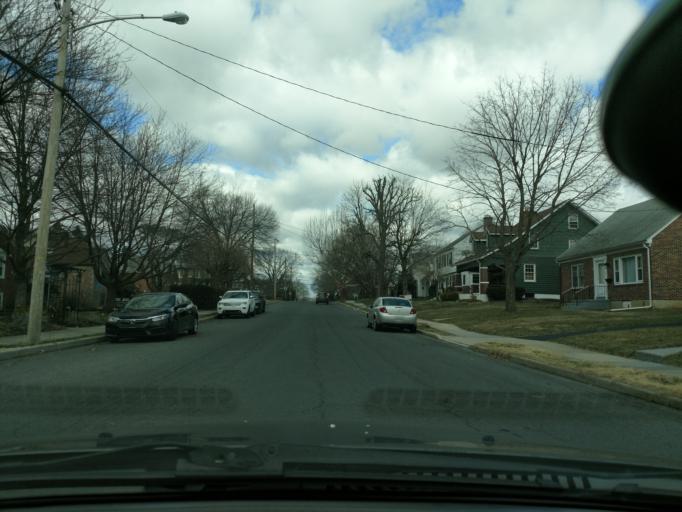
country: US
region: Pennsylvania
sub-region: Lebanon County
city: Hebron
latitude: 40.3356
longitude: -76.4060
